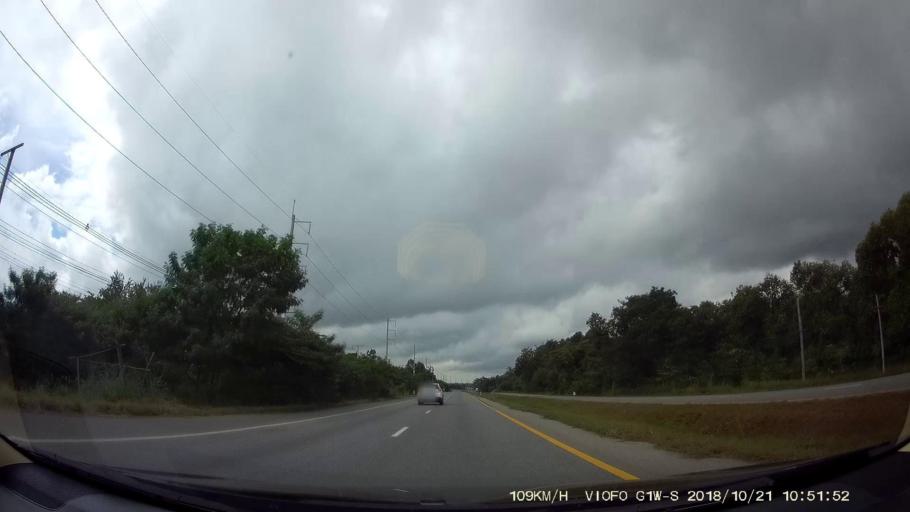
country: TH
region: Chaiyaphum
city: Khon Sawan
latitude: 15.9823
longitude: 102.1995
